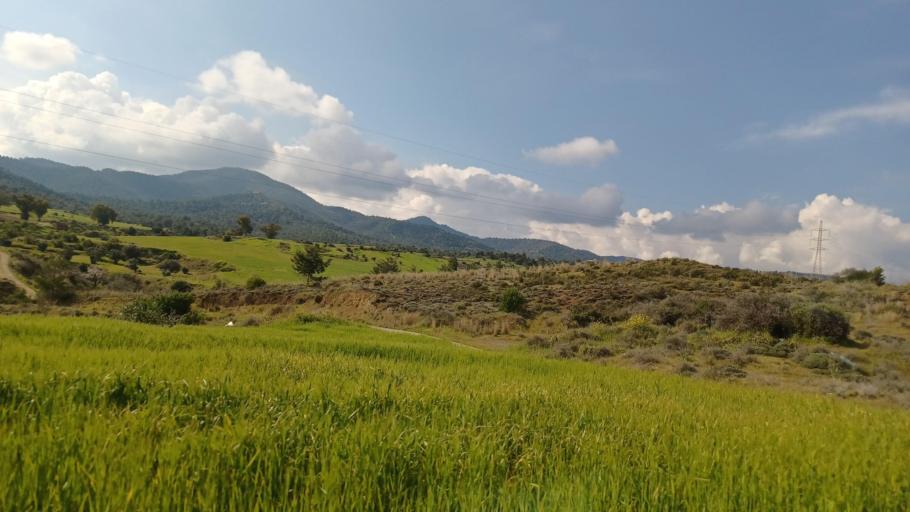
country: CY
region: Lefkosia
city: Kakopetria
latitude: 35.0816
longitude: 32.9514
